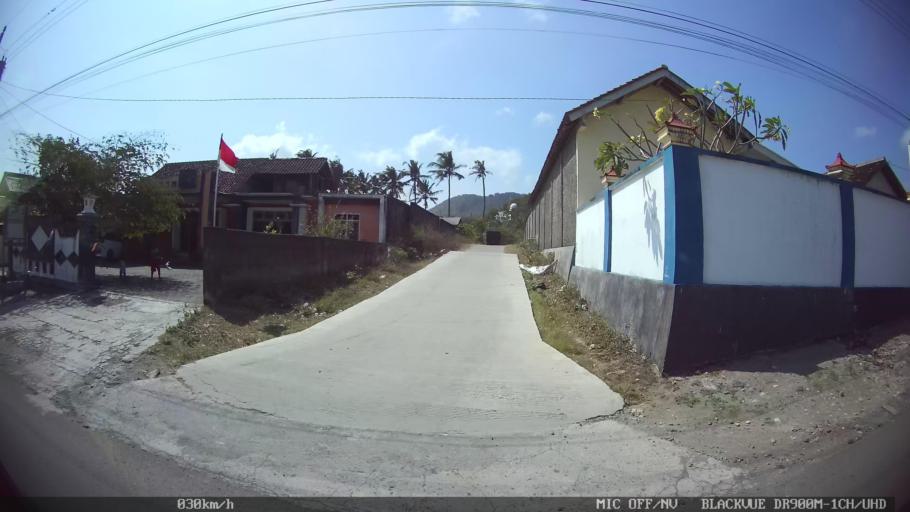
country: ID
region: Daerah Istimewa Yogyakarta
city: Pundong
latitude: -8.0194
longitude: 110.3230
